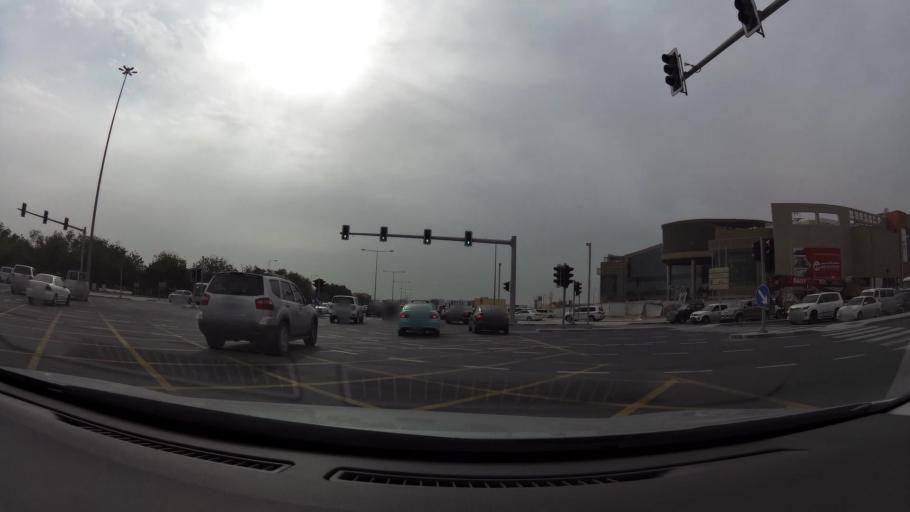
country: QA
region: Baladiyat ad Dawhah
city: Doha
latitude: 25.3354
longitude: 51.4823
